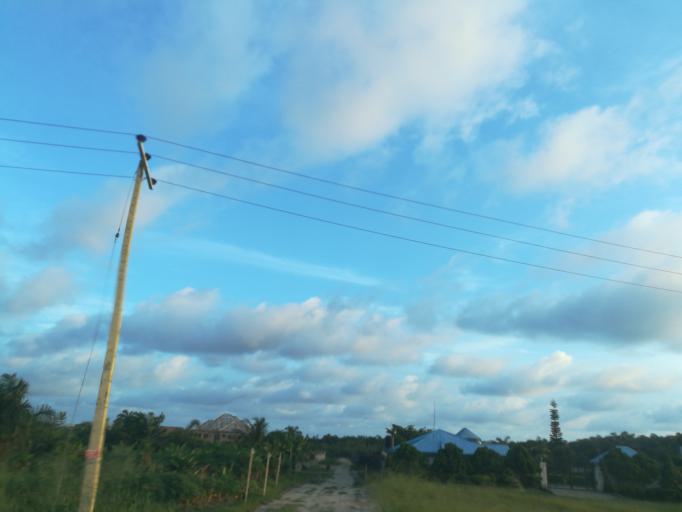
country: NG
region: Lagos
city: Badagry
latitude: 6.4744
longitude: 3.0156
